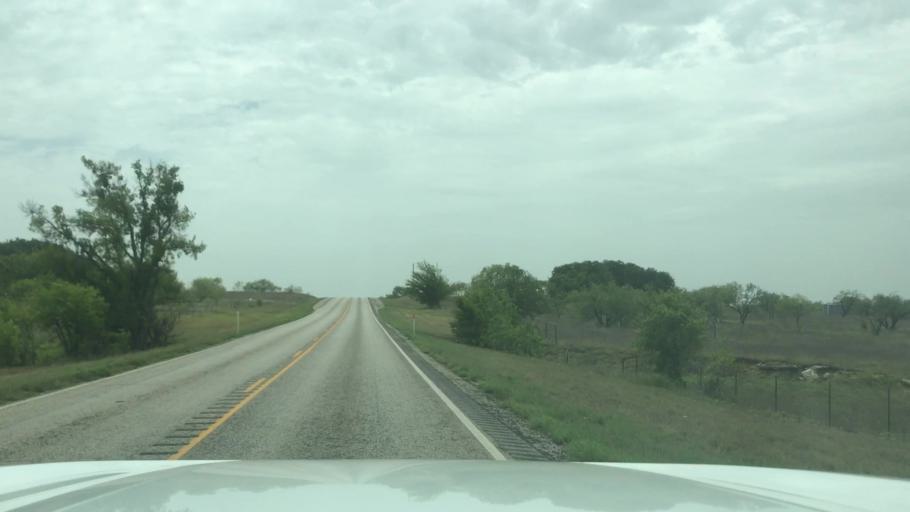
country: US
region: Texas
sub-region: Hamilton County
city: Hico
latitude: 32.0519
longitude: -98.1670
